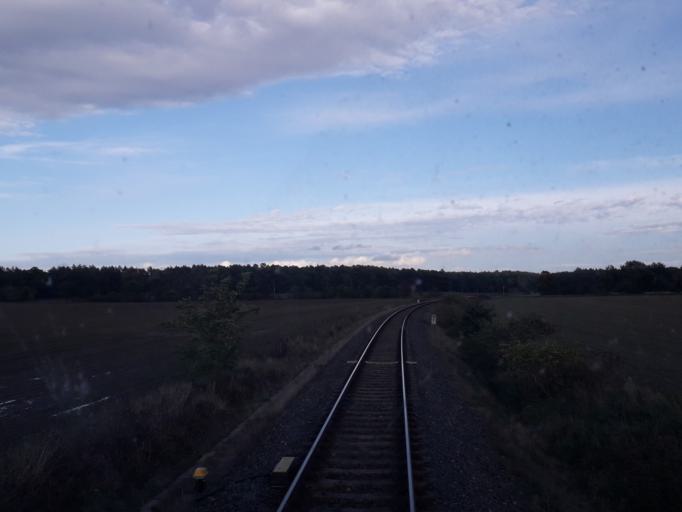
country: DE
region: Brandenburg
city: Perleberg
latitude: 53.0848
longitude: 11.9224
